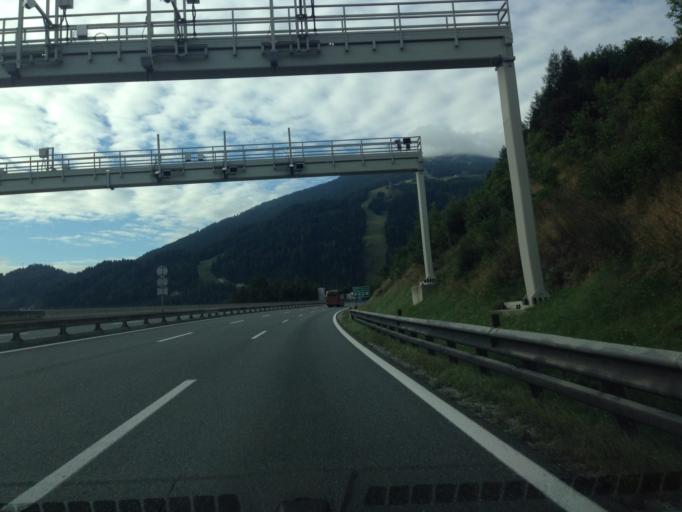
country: AT
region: Tyrol
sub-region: Politischer Bezirk Innsbruck Land
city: Steinach am Brenner
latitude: 47.0959
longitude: 11.4624
